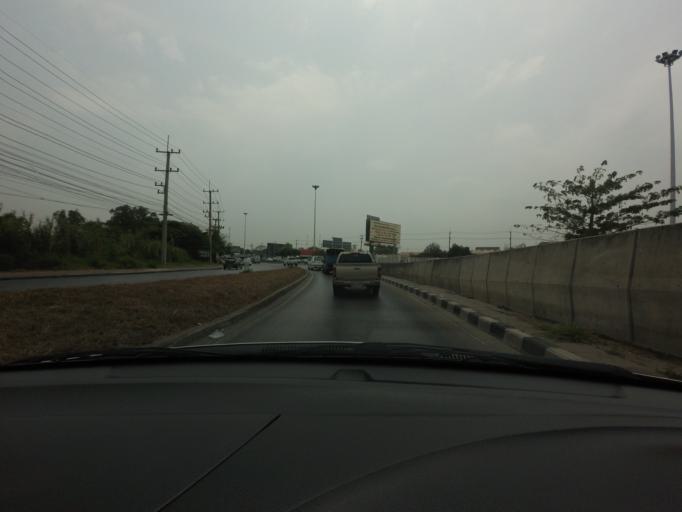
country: TH
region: Bangkok
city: Thawi Watthana
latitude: 13.7881
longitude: 100.3301
